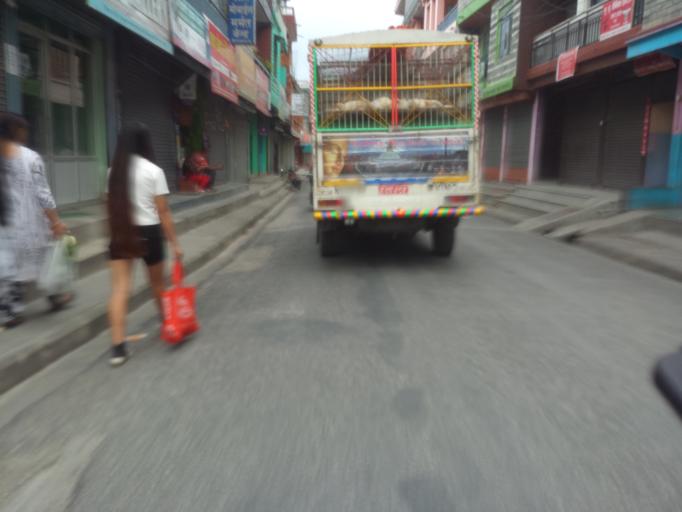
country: NP
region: Western Region
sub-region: Gandaki Zone
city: Pokhara
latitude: 28.2017
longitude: 83.9955
